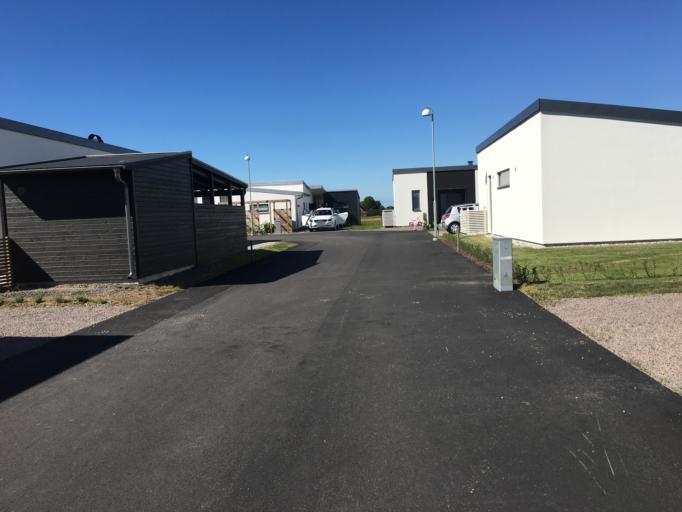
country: SE
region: Skane
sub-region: Hoganas Kommun
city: Hoganas
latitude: 56.1504
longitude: 12.5882
